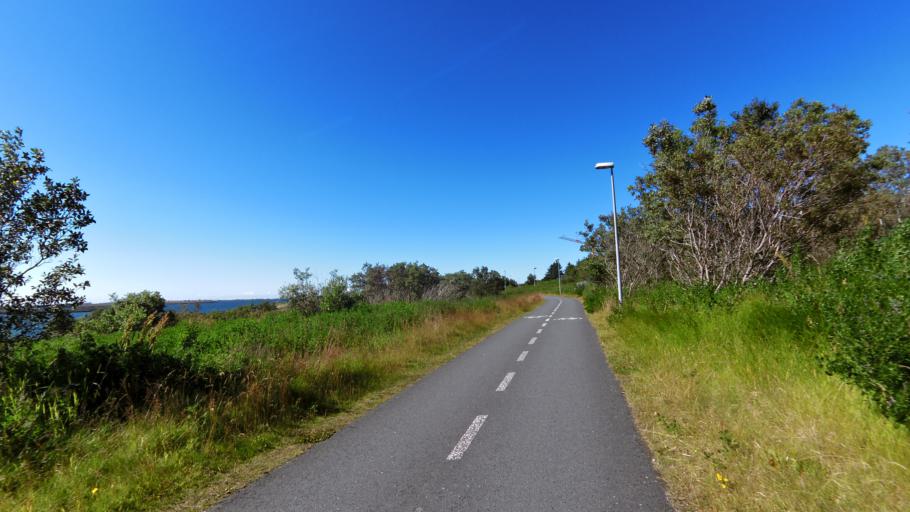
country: IS
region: Capital Region
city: Kopavogur
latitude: 64.1216
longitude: -21.9187
